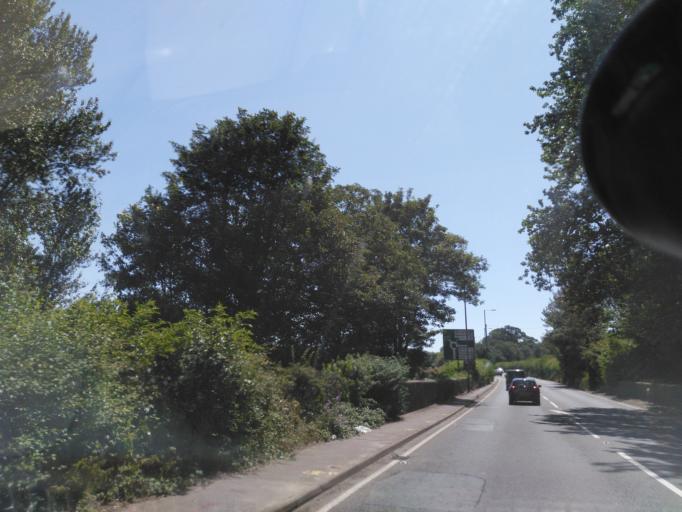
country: GB
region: England
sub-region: Bath and North East Somerset
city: Corston
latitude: 51.3887
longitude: -2.4339
